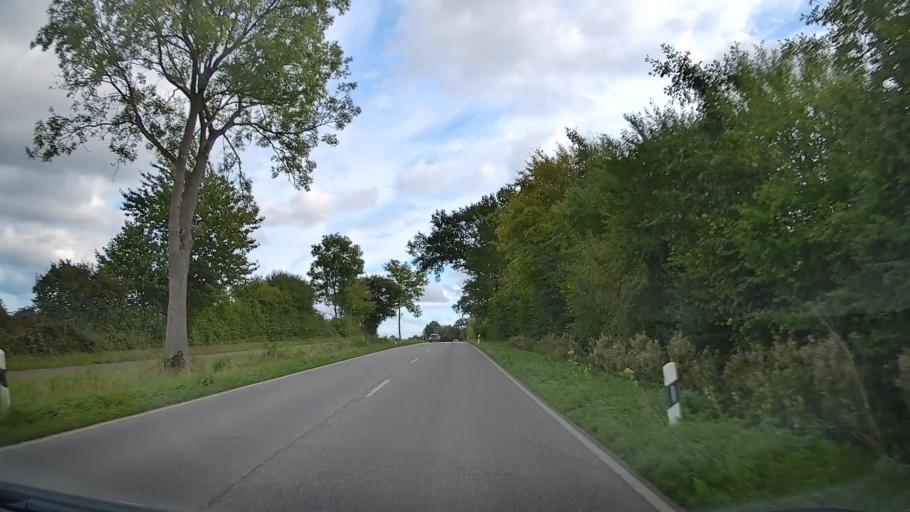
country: DE
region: Schleswig-Holstein
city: Niesgrau
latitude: 54.7532
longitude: 9.8100
